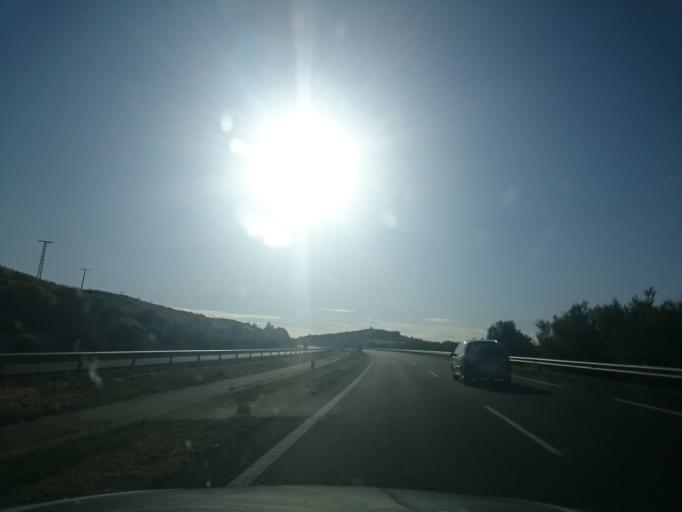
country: ES
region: Castille and Leon
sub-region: Provincia de Burgos
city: Rabe de las Calzadas
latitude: 42.3706
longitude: -3.8536
